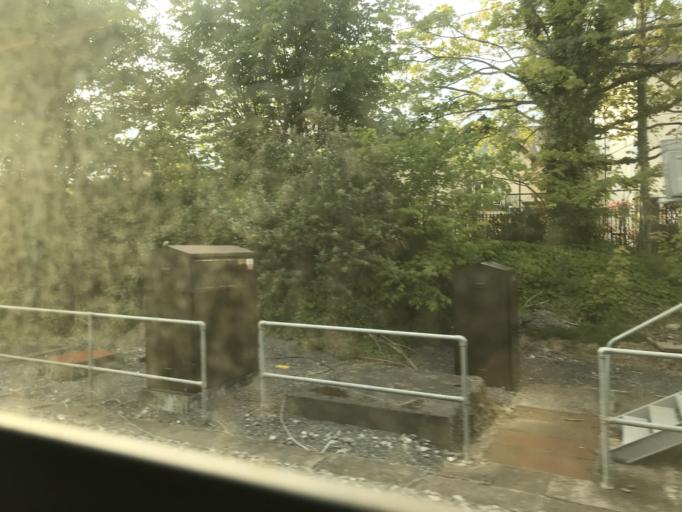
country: IE
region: Leinster
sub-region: Fingal County
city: Howth
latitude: 53.3907
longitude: -6.0847
